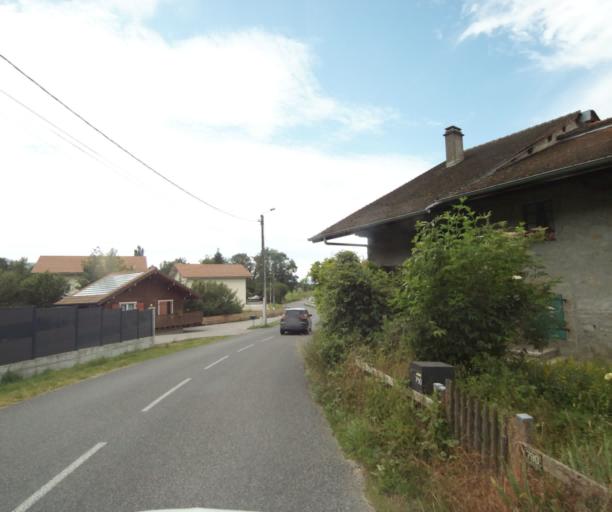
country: FR
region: Rhone-Alpes
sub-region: Departement de la Haute-Savoie
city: Bons-en-Chablais
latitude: 46.2662
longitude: 6.3866
